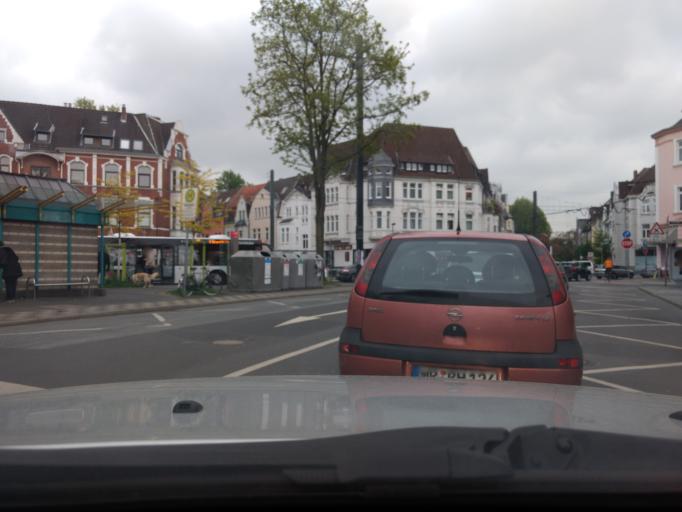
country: DE
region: North Rhine-Westphalia
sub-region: Regierungsbezirk Dusseldorf
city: Dusseldorf
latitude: 51.2315
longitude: 6.7470
